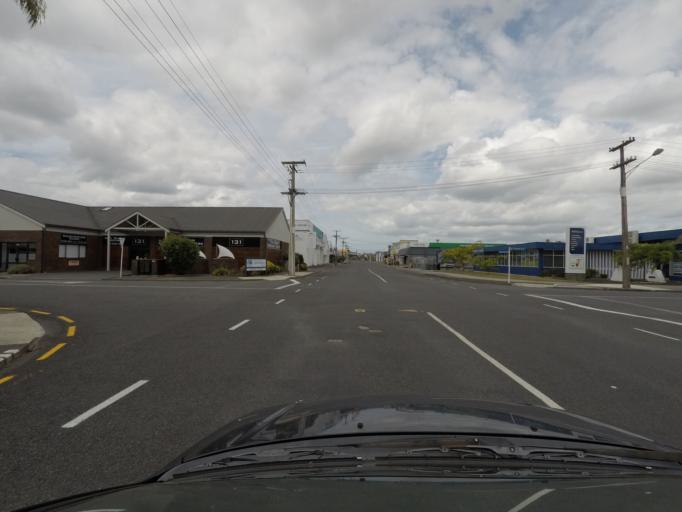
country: NZ
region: Northland
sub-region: Whangarei
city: Whangarei
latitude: -35.7265
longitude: 174.3278
